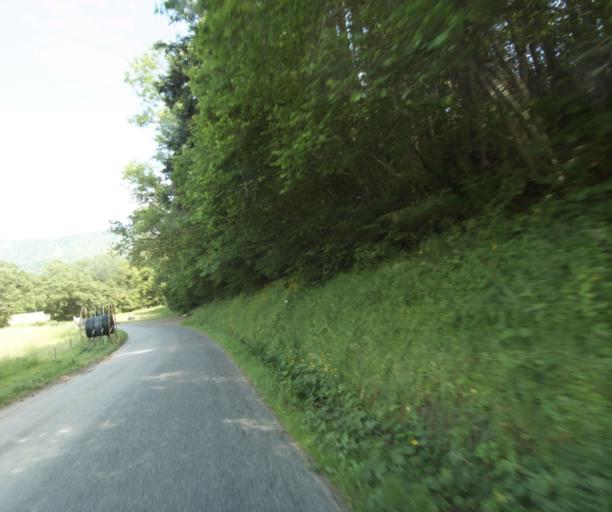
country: FR
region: Rhone-Alpes
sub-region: Departement de la Haute-Savoie
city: Bons-en-Chablais
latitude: 46.2777
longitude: 6.4195
